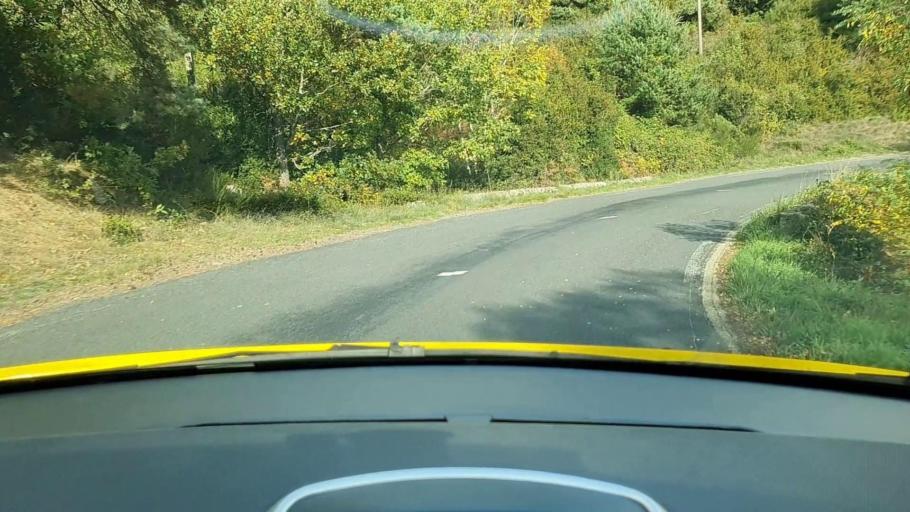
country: FR
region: Languedoc-Roussillon
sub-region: Departement de la Lozere
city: Meyrueis
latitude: 44.0653
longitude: 3.4092
